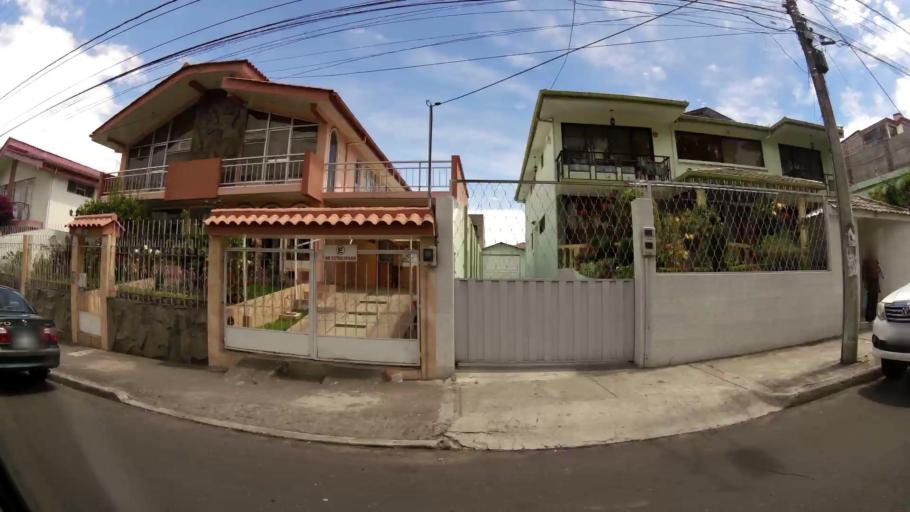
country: EC
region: Tungurahua
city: Ambato
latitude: -1.2538
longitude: -78.6355
